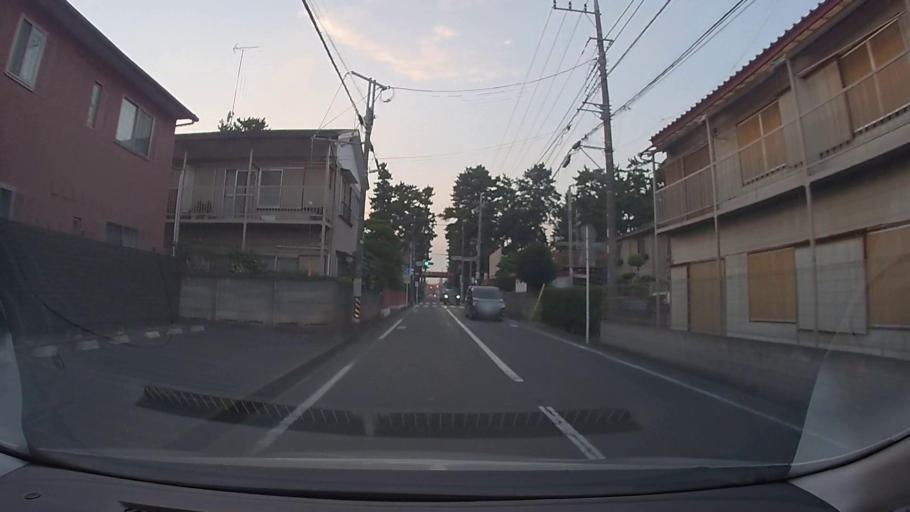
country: JP
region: Kanagawa
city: Minami-rinkan
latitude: 35.4987
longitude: 139.4451
